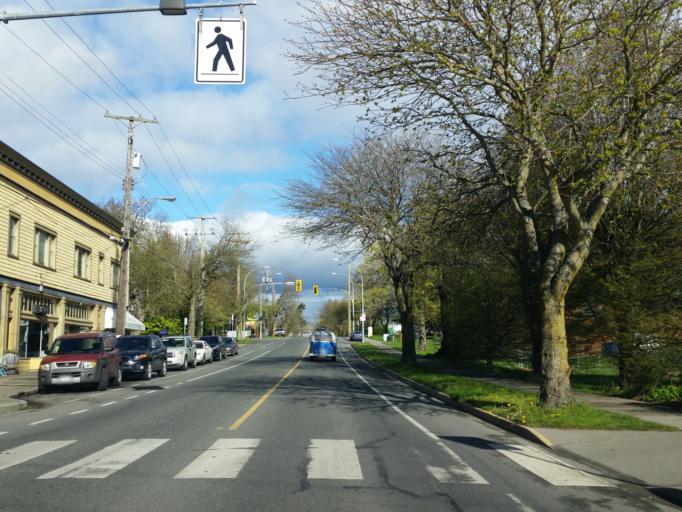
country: CA
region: British Columbia
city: Victoria
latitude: 48.4365
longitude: -123.3879
